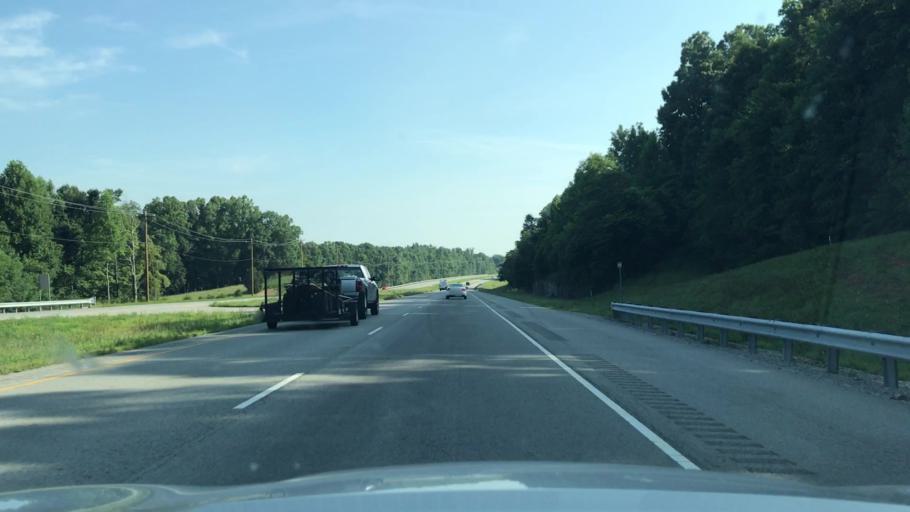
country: US
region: Tennessee
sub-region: Overton County
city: Livingston
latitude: 36.3168
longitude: -85.3632
